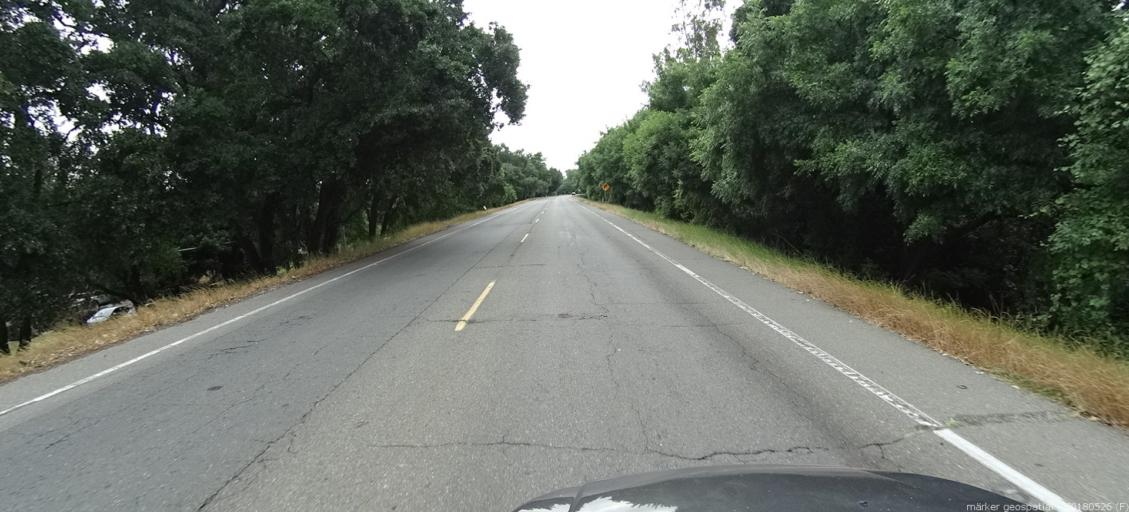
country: US
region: California
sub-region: Sacramento County
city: Sacramento
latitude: 38.6084
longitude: -121.4946
